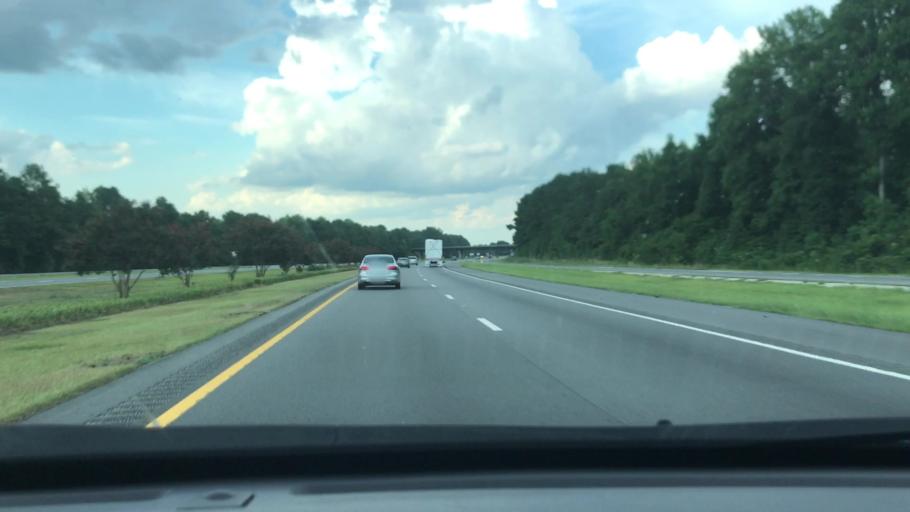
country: US
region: North Carolina
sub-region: Cumberland County
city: Vander
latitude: 35.0489
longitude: -78.8013
